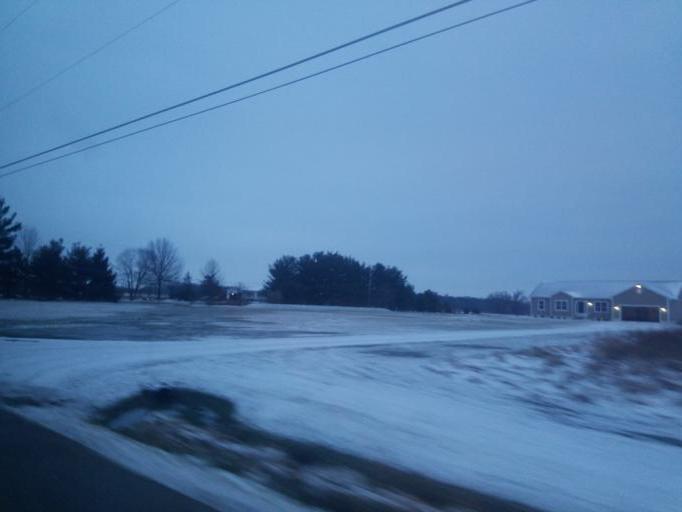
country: US
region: Ohio
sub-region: Delaware County
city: Sunbury
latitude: 40.2050
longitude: -82.8429
